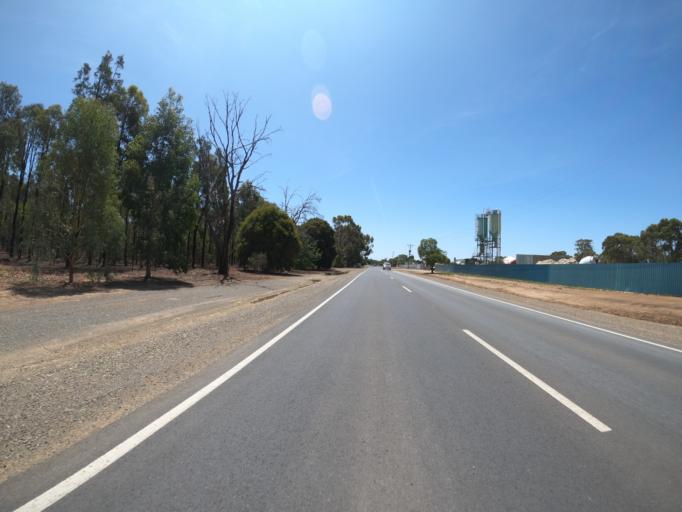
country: AU
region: Victoria
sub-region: Moira
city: Yarrawonga
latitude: -36.0249
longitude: 145.9955
